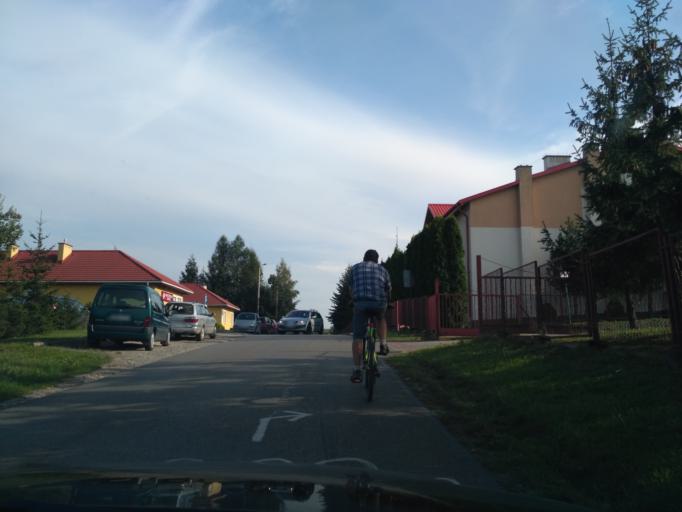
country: PL
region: Subcarpathian Voivodeship
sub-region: Powiat rzeszowski
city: Niechobrz
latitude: 49.9967
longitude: 21.8737
